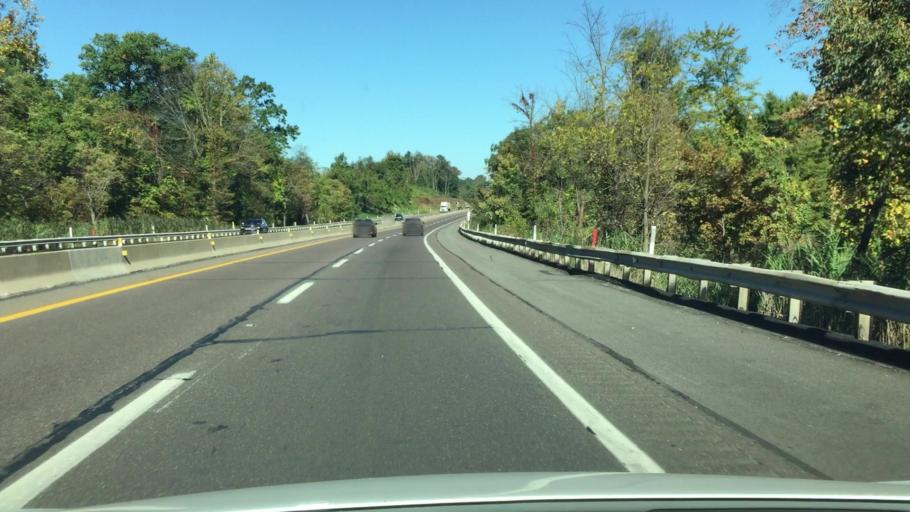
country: US
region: Pennsylvania
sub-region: Chester County
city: Elverson
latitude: 40.1258
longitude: -75.7852
